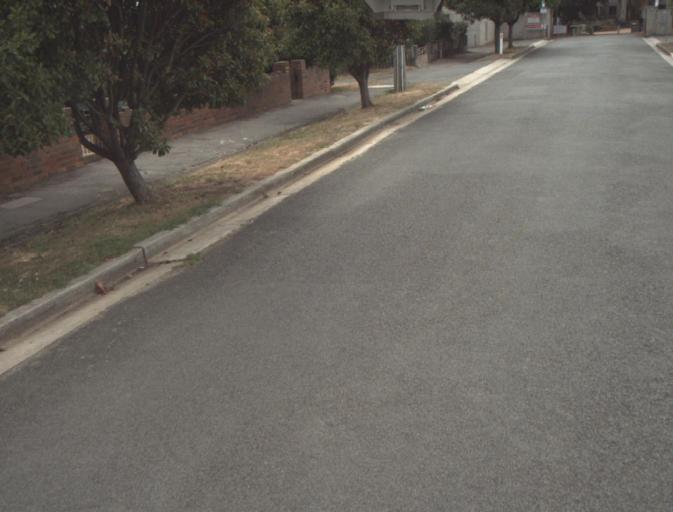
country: AU
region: Tasmania
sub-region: Launceston
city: Newnham
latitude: -41.4045
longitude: 147.1232
